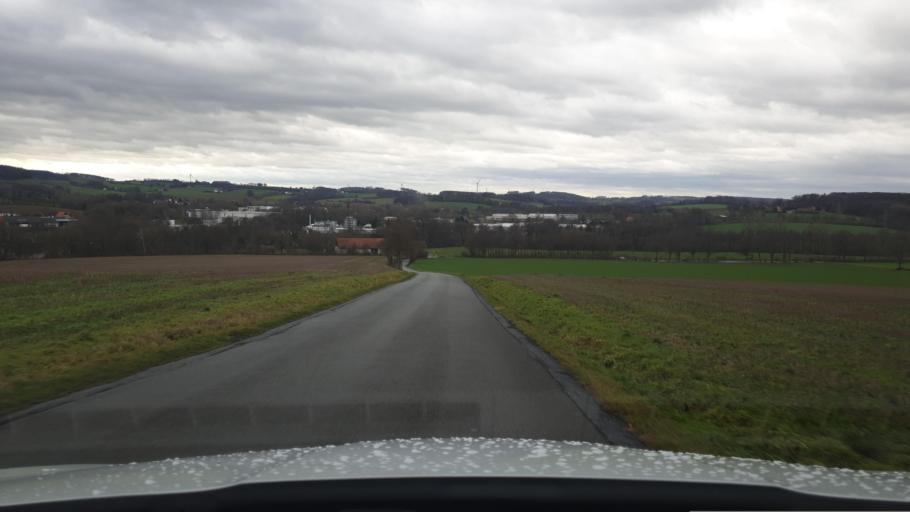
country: DE
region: North Rhine-Westphalia
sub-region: Regierungsbezirk Detmold
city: Vlotho
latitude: 52.1457
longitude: 8.8257
